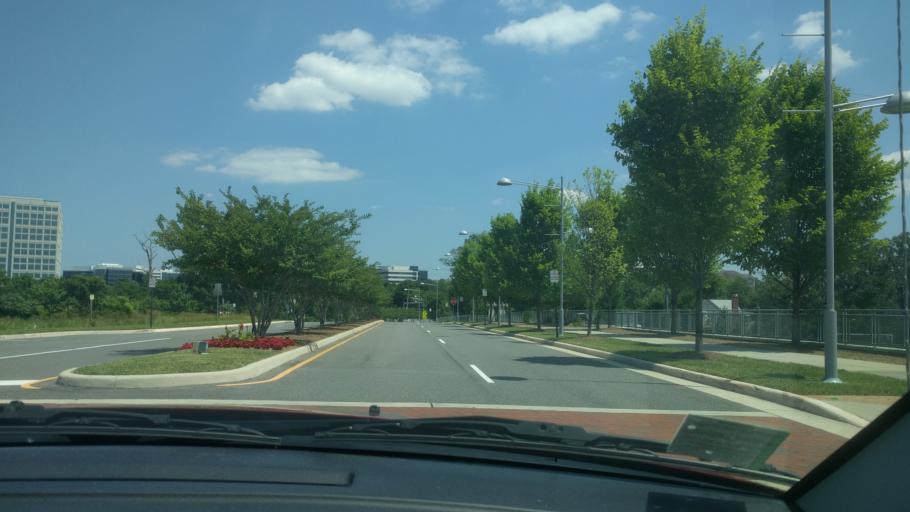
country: US
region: Virginia
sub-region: Fairfax County
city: Floris
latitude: 38.9548
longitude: -77.4095
